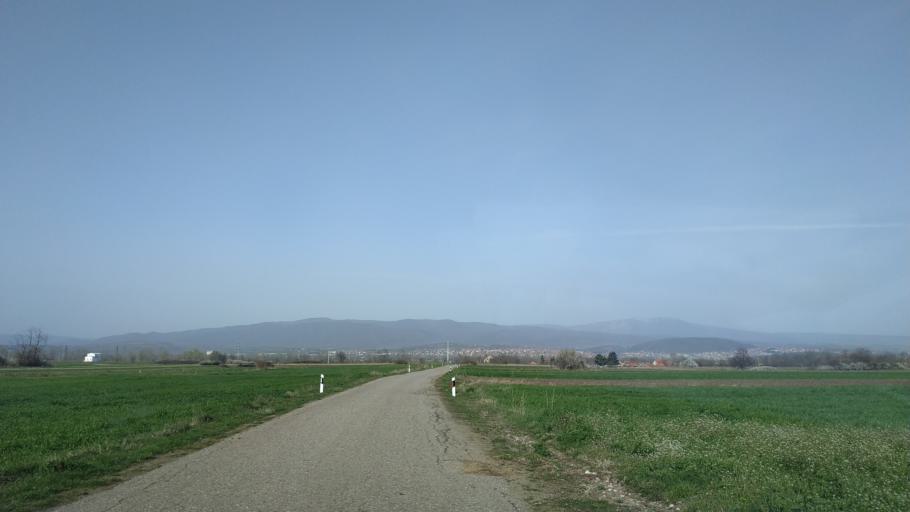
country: RS
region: Central Serbia
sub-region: Nisavski Okrug
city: Aleksinac
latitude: 43.5222
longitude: 21.6551
